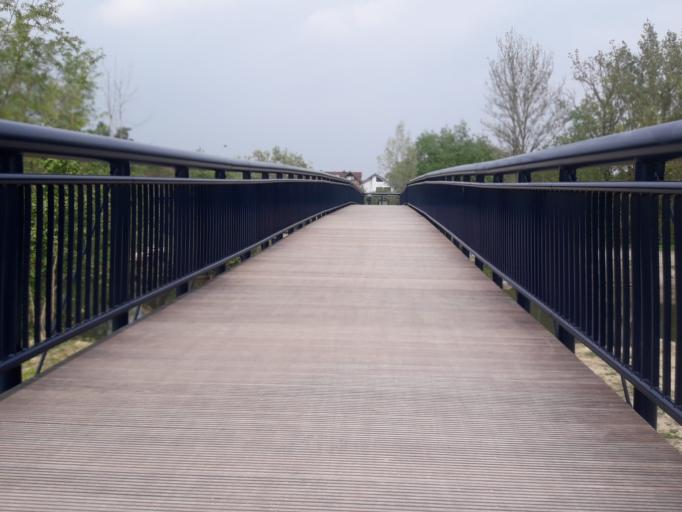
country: DE
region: North Rhine-Westphalia
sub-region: Regierungsbezirk Detmold
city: Paderborn
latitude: 51.7488
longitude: 8.7062
